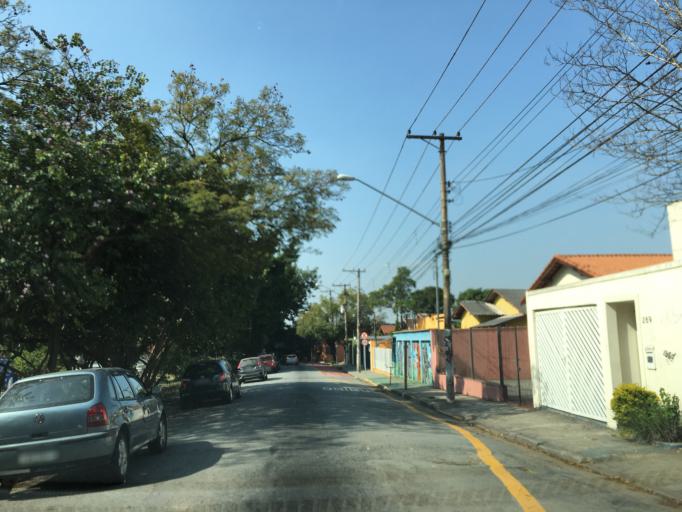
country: BR
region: Sao Paulo
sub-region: Osasco
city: Osasco
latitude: -23.5775
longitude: -46.7232
